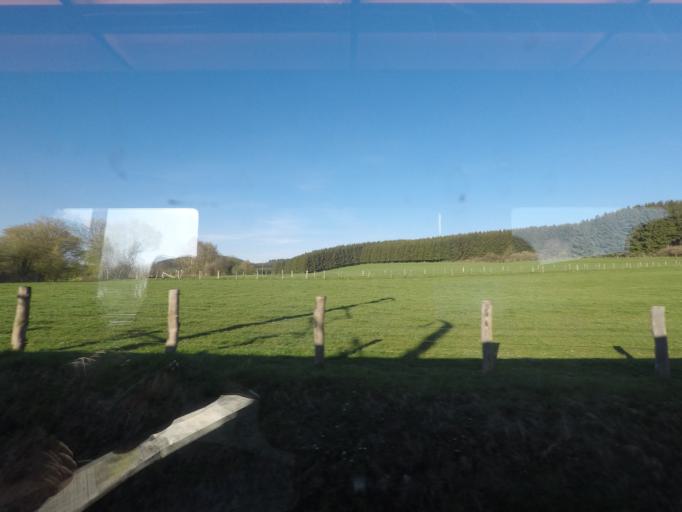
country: BE
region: Wallonia
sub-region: Province du Luxembourg
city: Leglise
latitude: 49.7954
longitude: 5.4977
